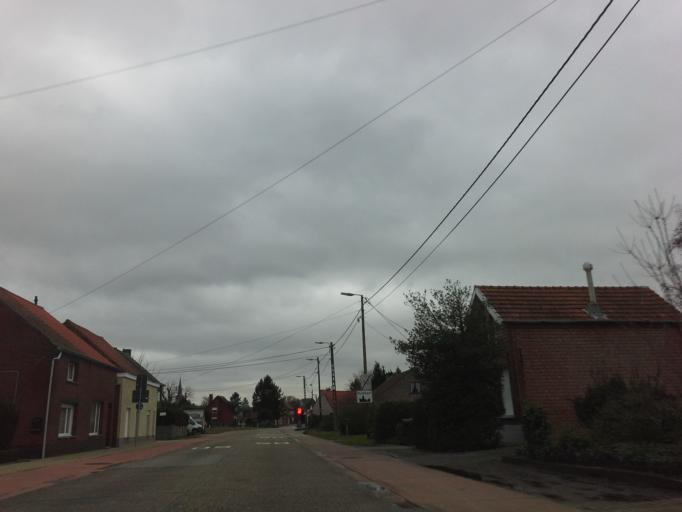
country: BE
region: Flanders
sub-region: Provincie Antwerpen
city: Hulshout
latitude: 51.0794
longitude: 4.7843
